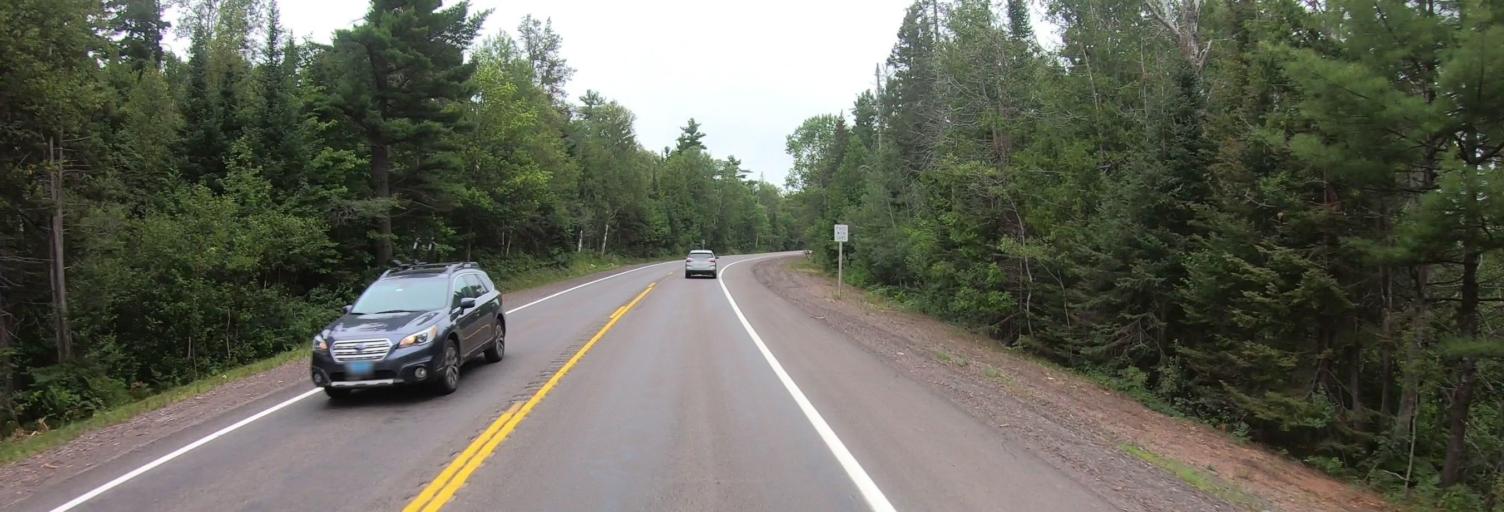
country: US
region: Michigan
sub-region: Keweenaw County
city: Eagle River
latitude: 47.3728
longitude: -88.3046
